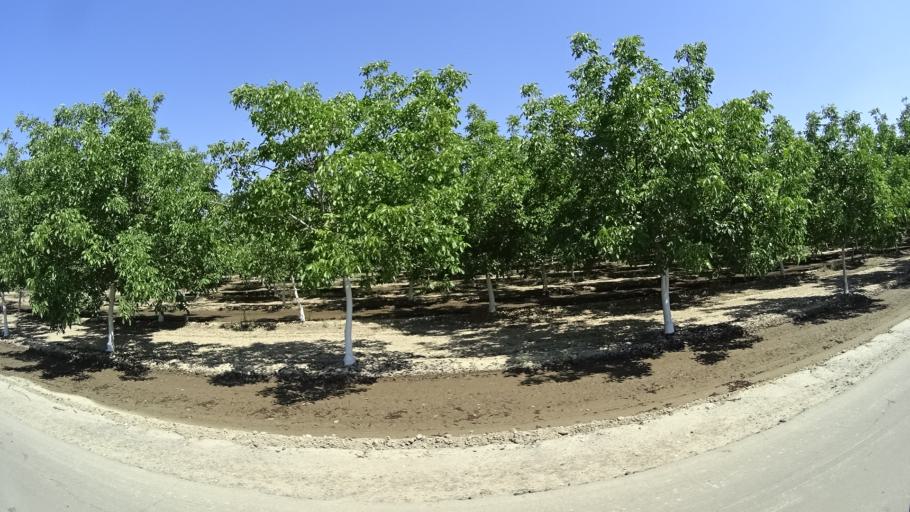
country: US
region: California
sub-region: Fresno County
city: Laton
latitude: 36.4380
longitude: -119.6224
